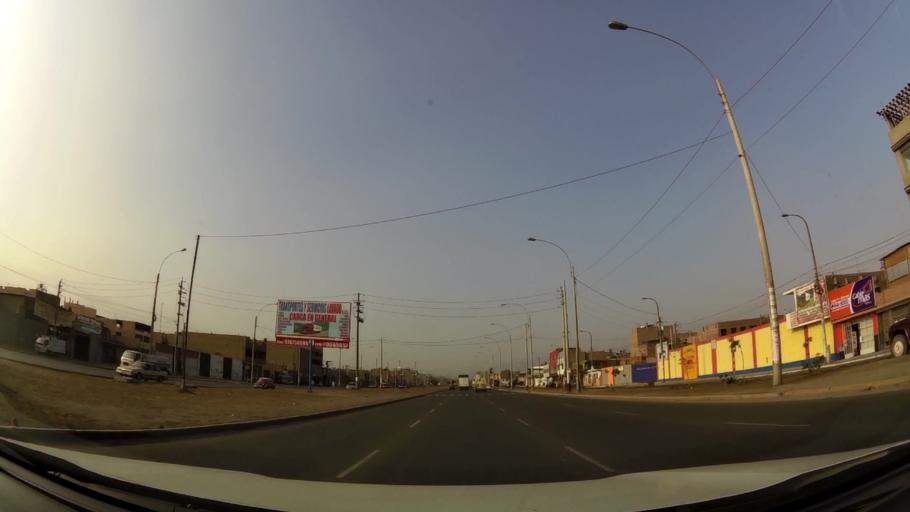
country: PE
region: Lima
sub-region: Lima
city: Independencia
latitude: -11.9865
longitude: -77.1022
